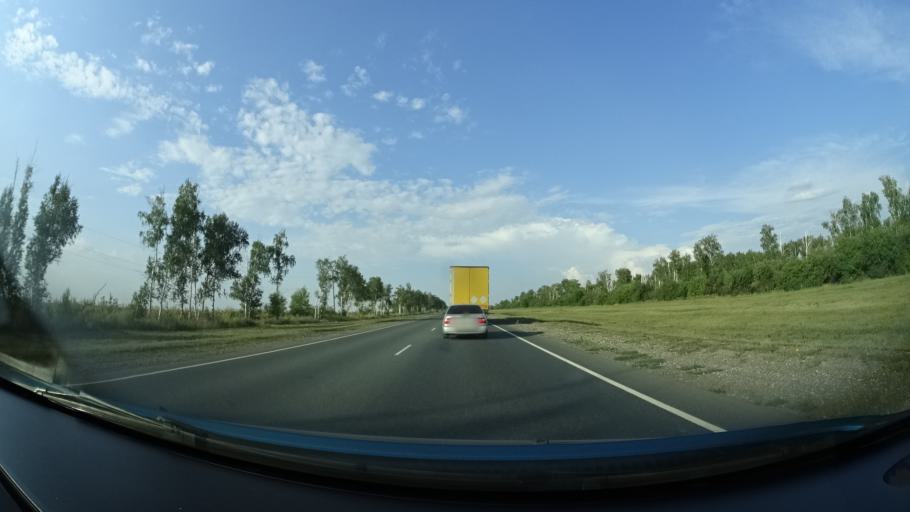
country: RU
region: Samara
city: Krasnyy Yar
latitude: 53.6628
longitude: 50.7568
